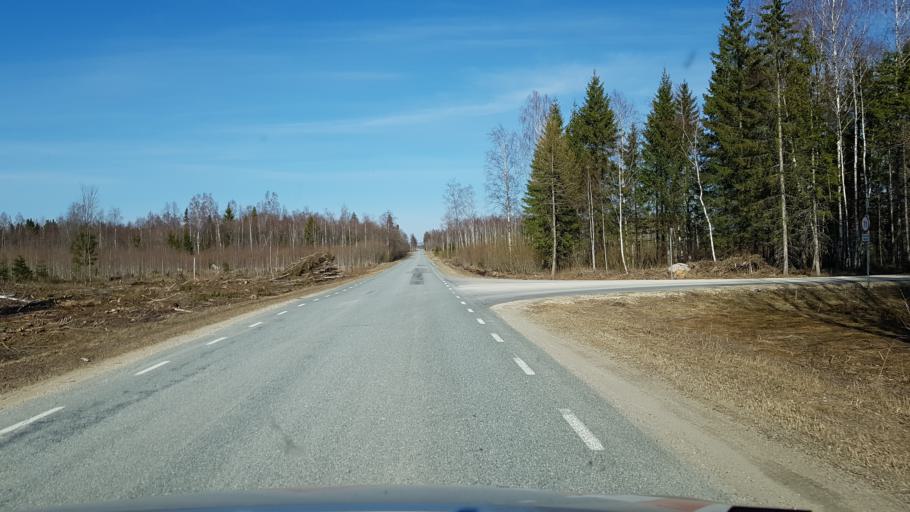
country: EE
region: Laeaene-Virumaa
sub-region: Rakke vald
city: Rakke
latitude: 59.0119
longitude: 26.3378
